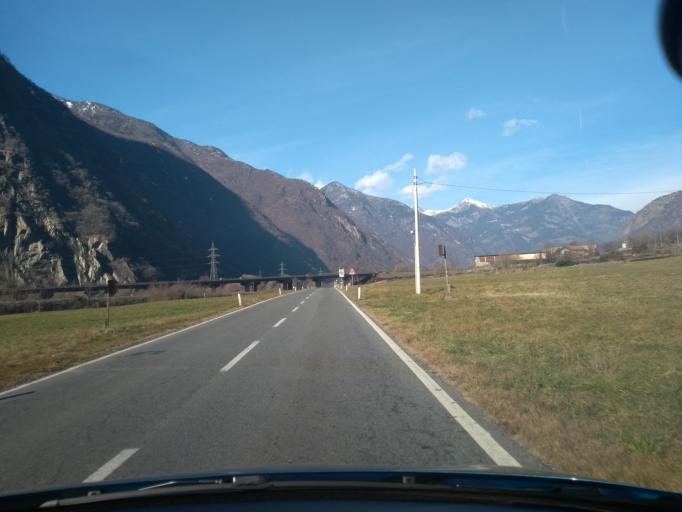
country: IT
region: Aosta Valley
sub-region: Valle d'Aosta
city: Hone
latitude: 45.6321
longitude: 7.7309
